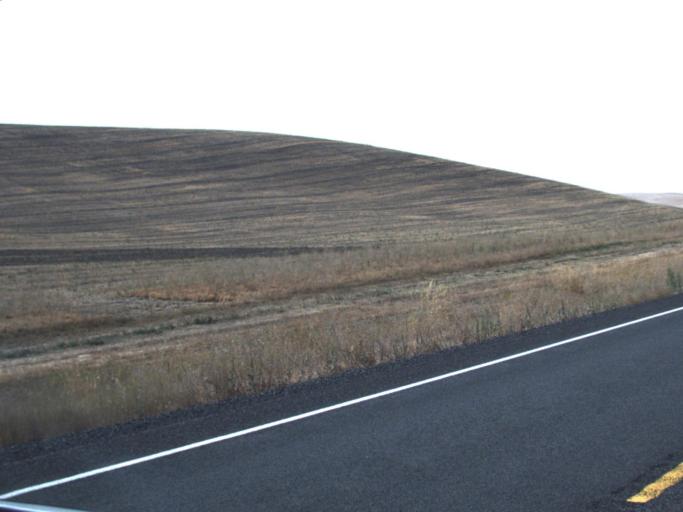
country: US
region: Washington
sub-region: Whitman County
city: Pullman
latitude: 46.8101
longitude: -117.1205
